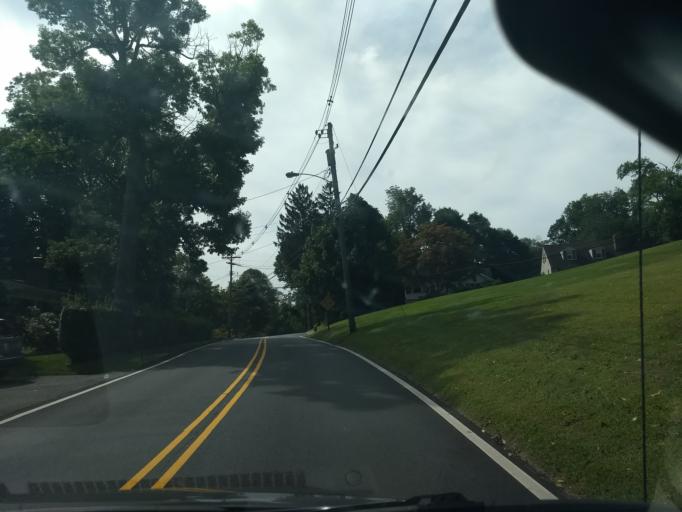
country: US
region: New Jersey
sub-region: Morris County
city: Morris Plains
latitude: 40.8221
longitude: -74.4939
